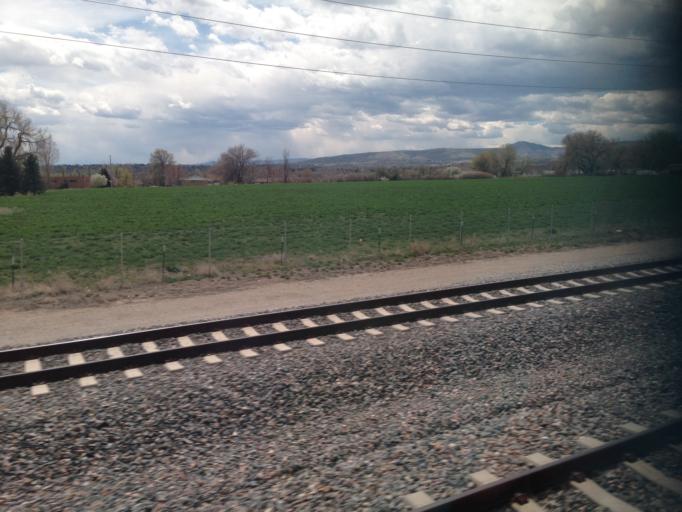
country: US
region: Colorado
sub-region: Jefferson County
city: Arvada
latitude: 39.7894
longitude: -105.1262
